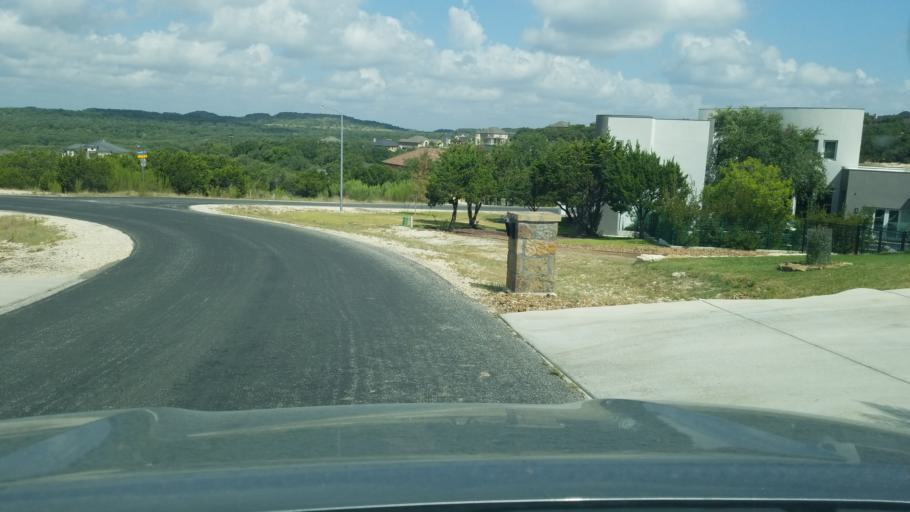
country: US
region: Texas
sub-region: Bexar County
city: Timberwood Park
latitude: 29.6856
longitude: -98.5182
